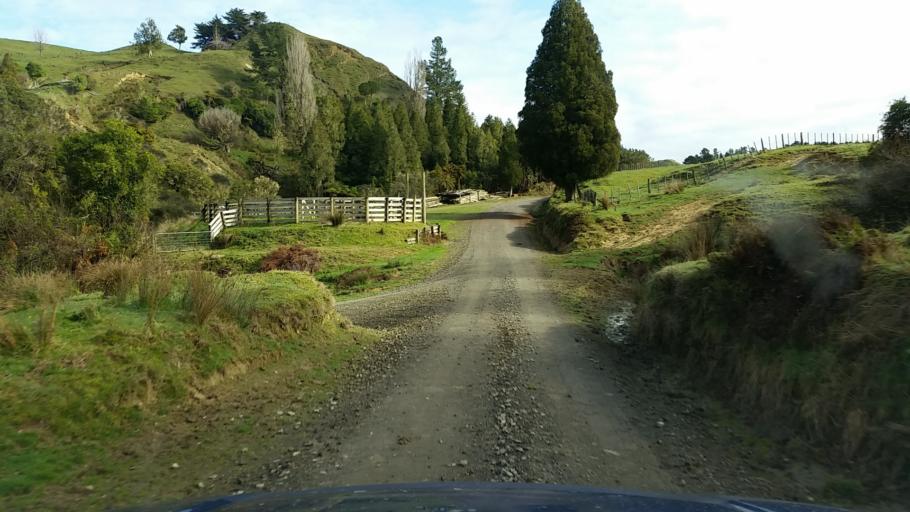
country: NZ
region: Taranaki
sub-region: New Plymouth District
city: Waitara
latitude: -39.1115
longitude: 174.8516
